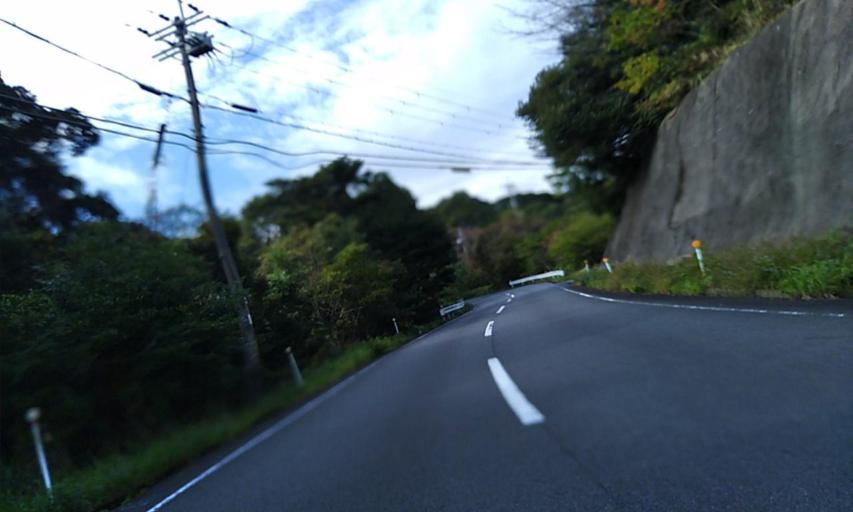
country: JP
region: Wakayama
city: Shingu
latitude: 33.4694
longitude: 135.8234
